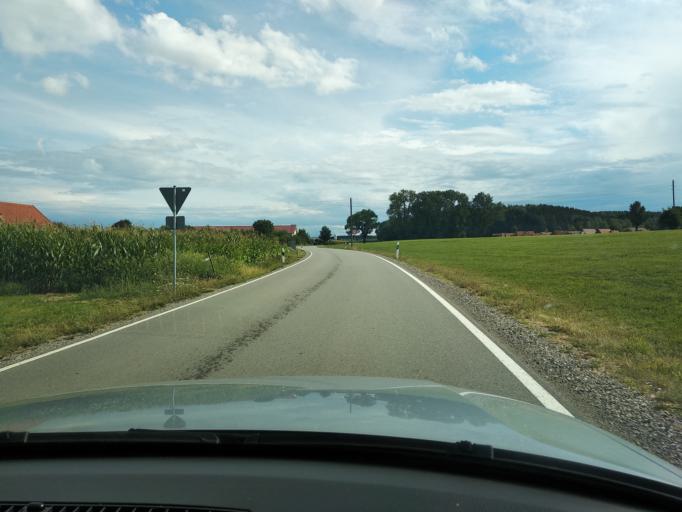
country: DE
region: Bavaria
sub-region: Swabia
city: Wolfertschwenden
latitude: 47.8788
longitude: 10.2350
